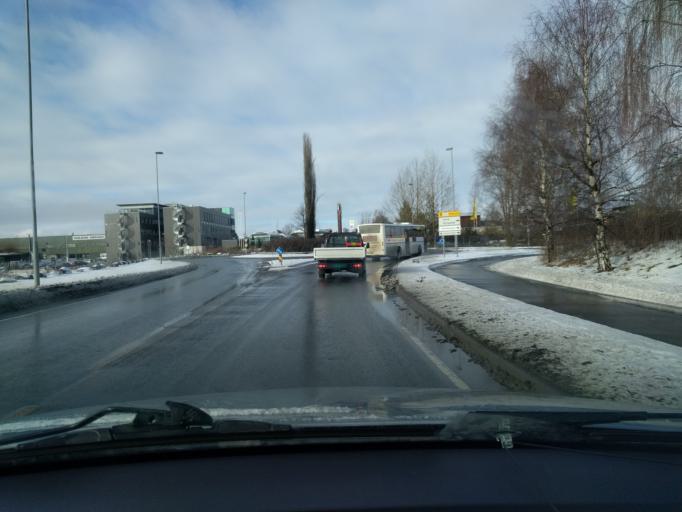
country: NO
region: Hedmark
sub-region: Hamar
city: Hamar
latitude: 60.7888
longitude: 11.0948
